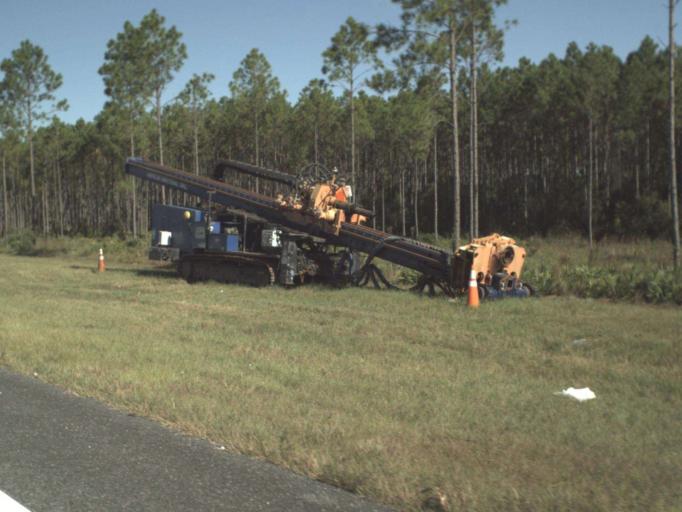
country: US
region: Florida
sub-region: Bay County
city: Laguna Beach
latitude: 30.2977
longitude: -86.0258
